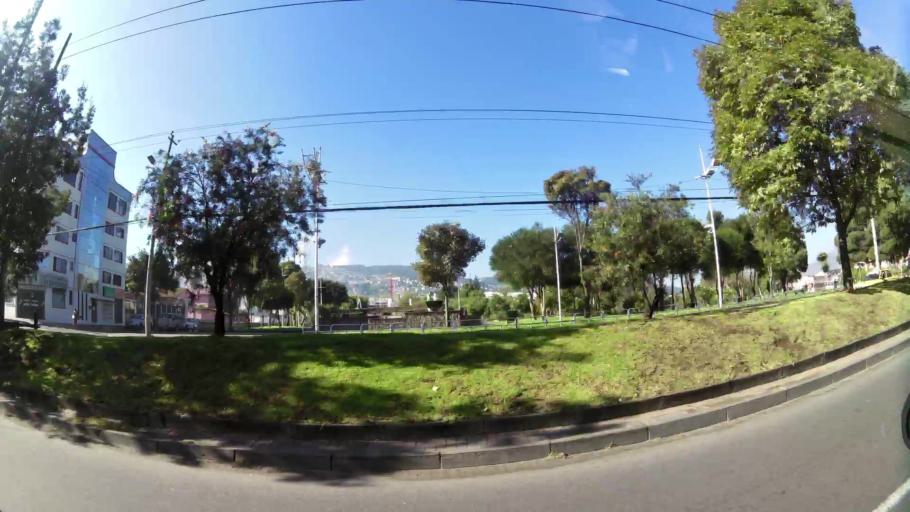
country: EC
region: Pichincha
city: Quito
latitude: -0.2469
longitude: -78.5234
